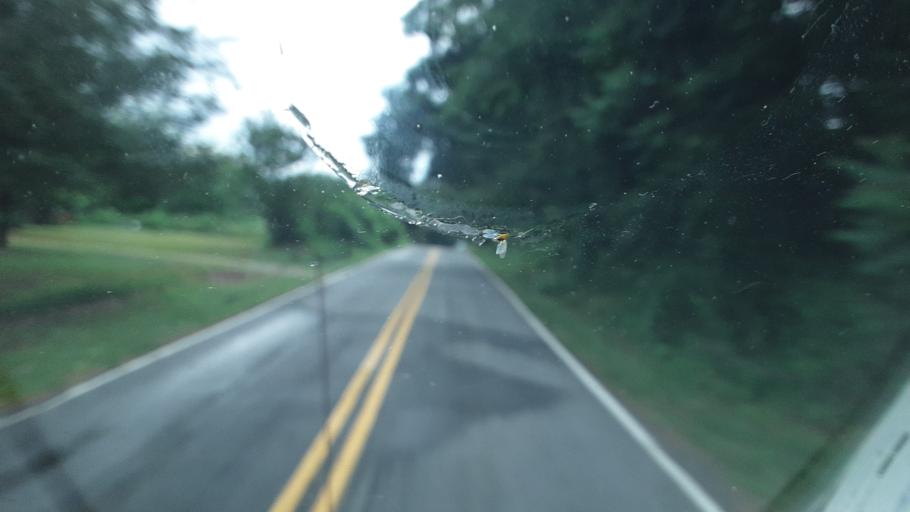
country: US
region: North Carolina
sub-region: Yadkin County
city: Jonesville
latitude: 36.0827
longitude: -80.8401
